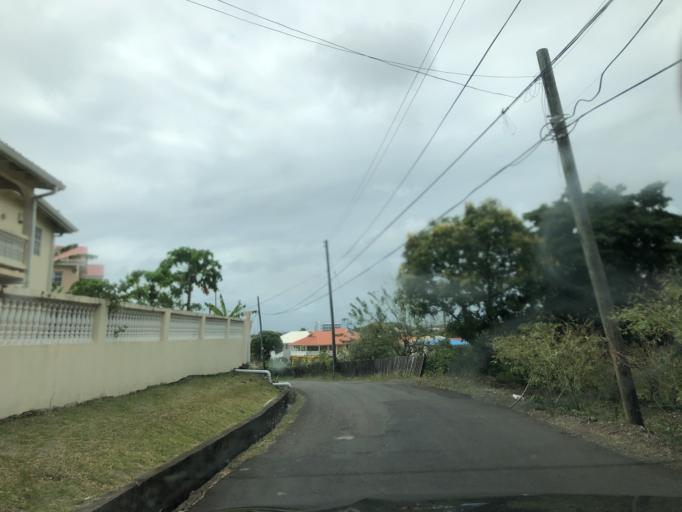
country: LC
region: Gros-Islet
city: Gros Islet
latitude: 14.0666
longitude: -60.9457
